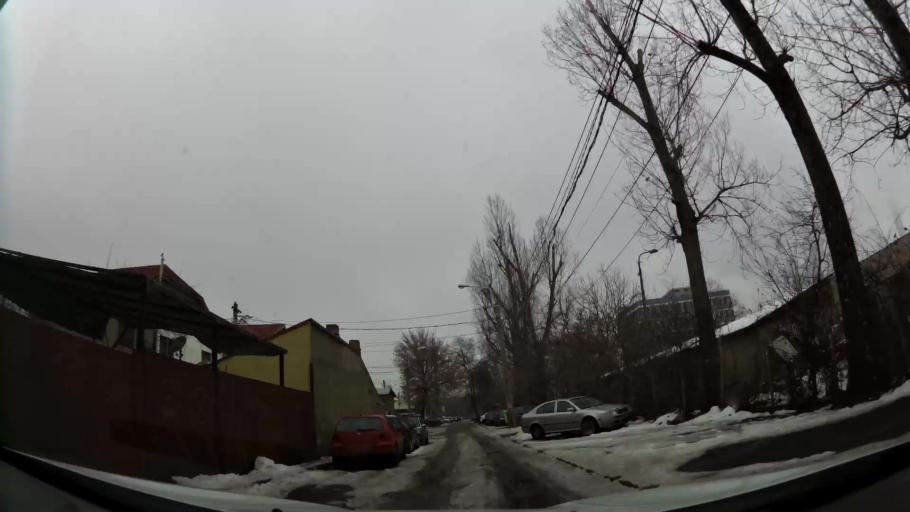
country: RO
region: Ilfov
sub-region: Comuna Popesti-Leordeni
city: Popesti-Leordeni
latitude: 44.4043
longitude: 26.1474
